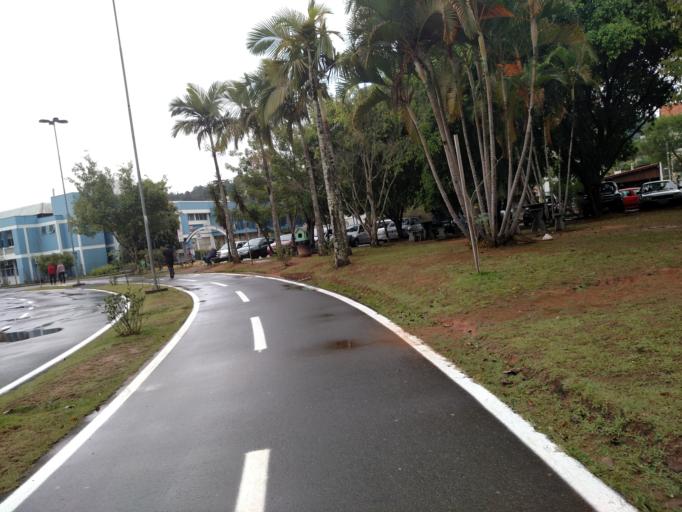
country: BR
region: Santa Catarina
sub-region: Blumenau
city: Blumenau
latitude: -26.9141
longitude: -49.0876
